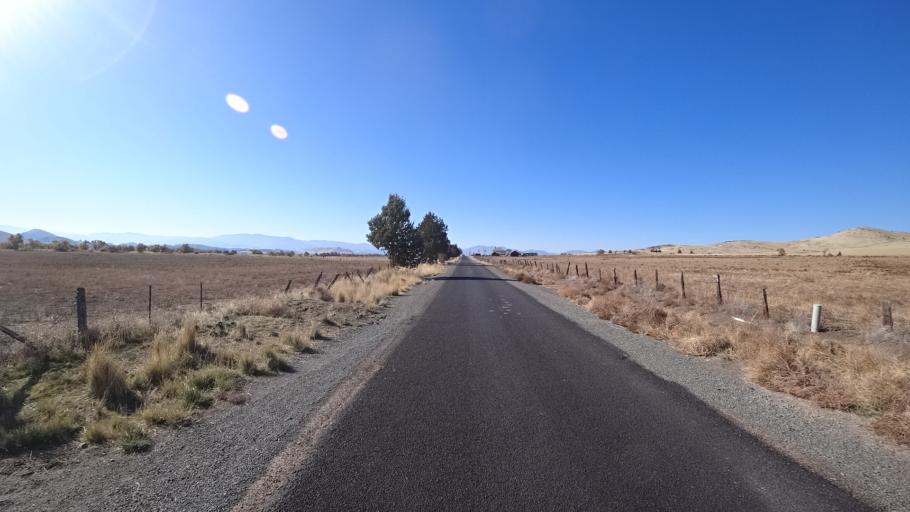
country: US
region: California
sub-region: Siskiyou County
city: Montague
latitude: 41.7263
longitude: -122.3751
